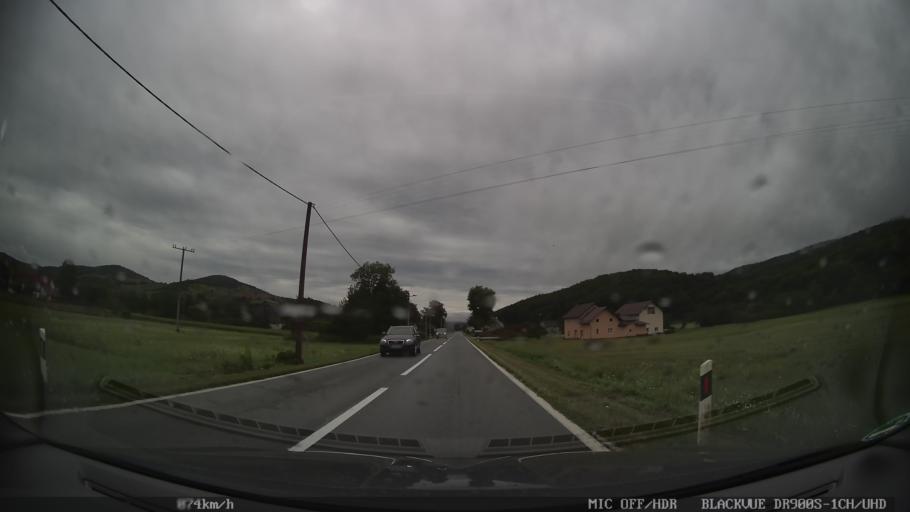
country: HR
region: Licko-Senjska
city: Brinje
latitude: 44.9371
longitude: 15.1276
